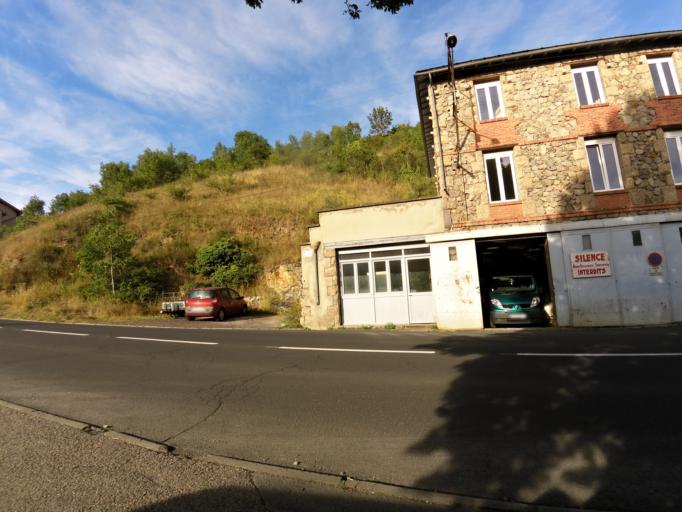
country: FR
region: Auvergne
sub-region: Departement du Puy-de-Dome
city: Aydat
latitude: 45.5848
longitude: 2.9921
